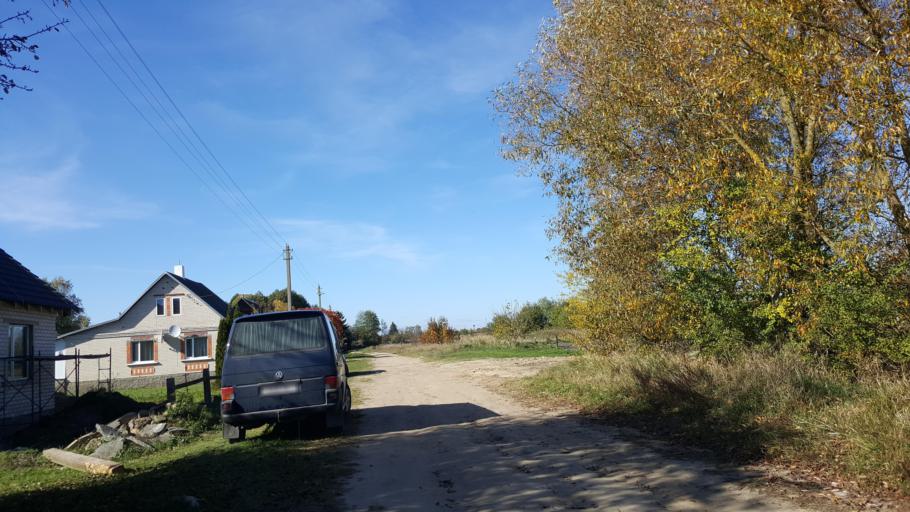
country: BY
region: Brest
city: Kamyanyets
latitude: 52.4031
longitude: 23.7889
